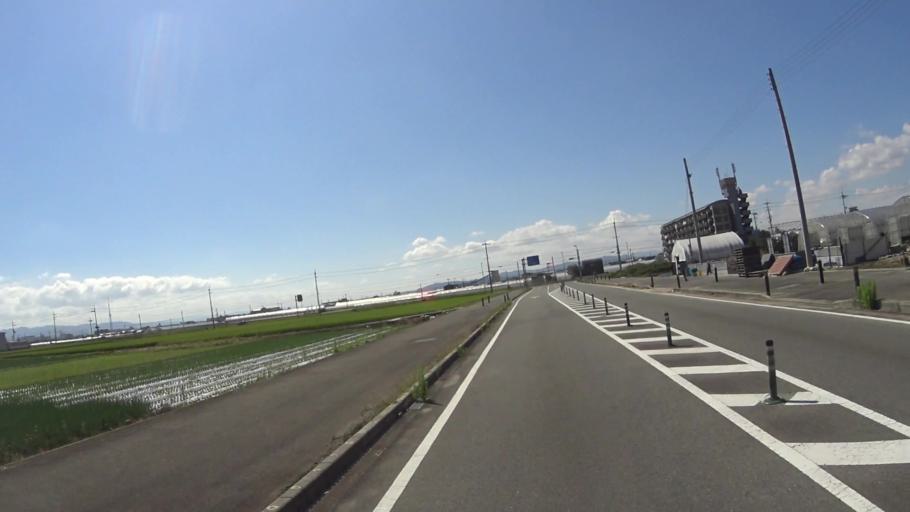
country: JP
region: Kyoto
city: Yawata
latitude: 34.8939
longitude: 135.7244
